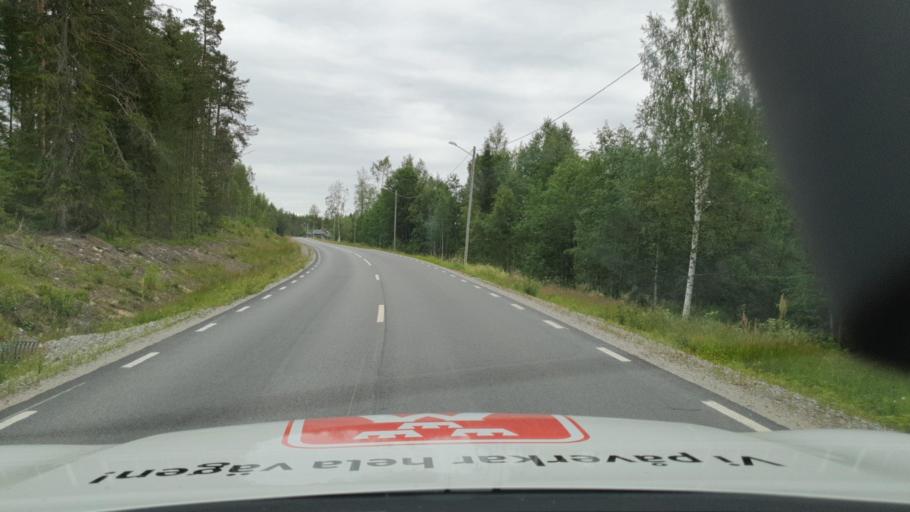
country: SE
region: Vaesterbotten
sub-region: Nordmalings Kommun
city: Nordmaling
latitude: 63.5200
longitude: 19.3599
